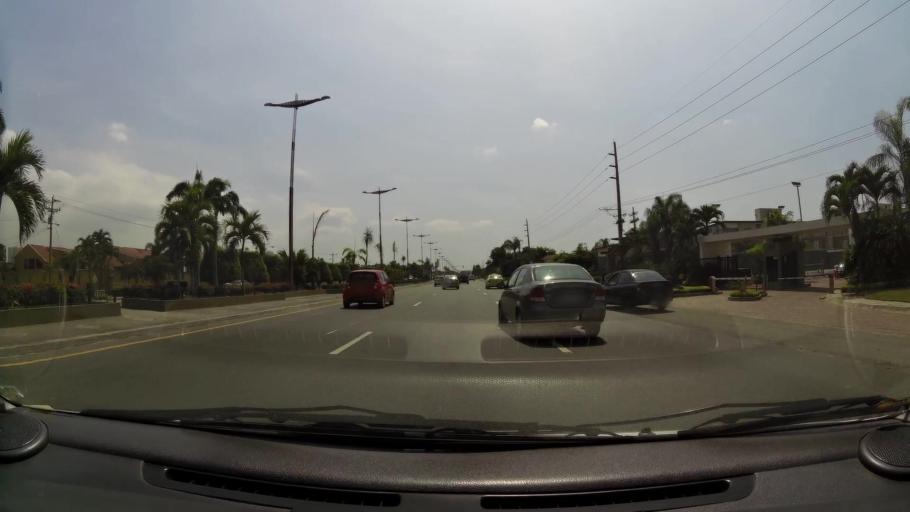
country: EC
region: Guayas
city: Eloy Alfaro
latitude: -2.1184
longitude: -79.8674
